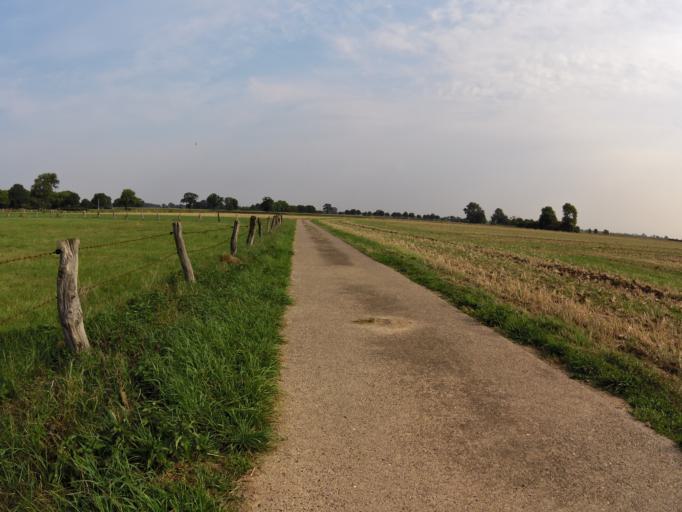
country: DE
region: Lower Saxony
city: Raddestorf
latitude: 52.4715
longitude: 9.0149
